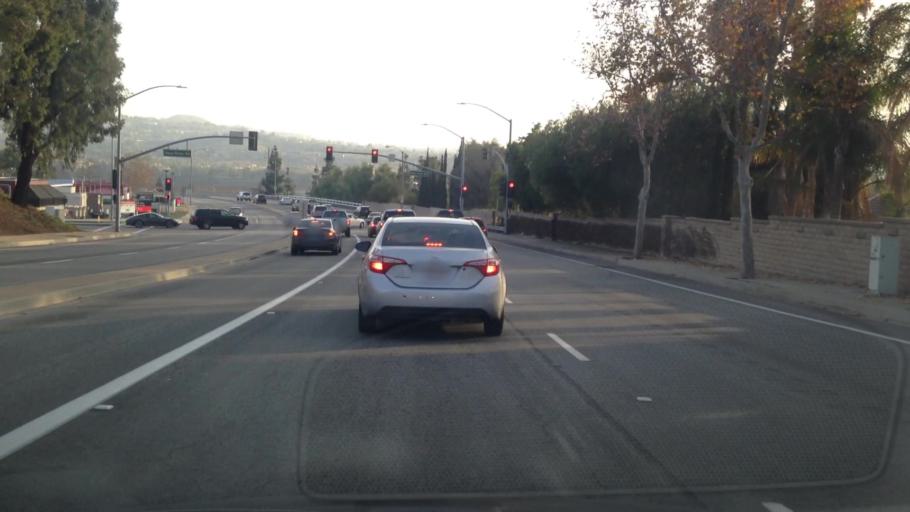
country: US
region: California
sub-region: Orange County
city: Yorba Linda
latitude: 33.8789
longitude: -117.7545
